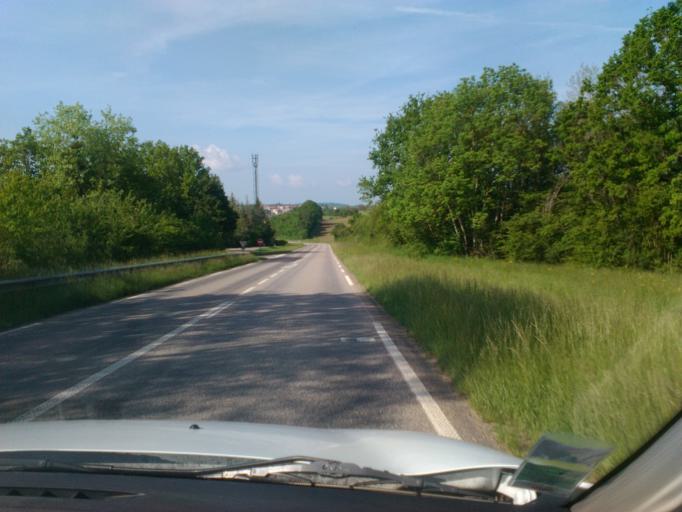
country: FR
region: Lorraine
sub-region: Departement des Vosges
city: Mirecourt
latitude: 48.3314
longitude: 6.1359
